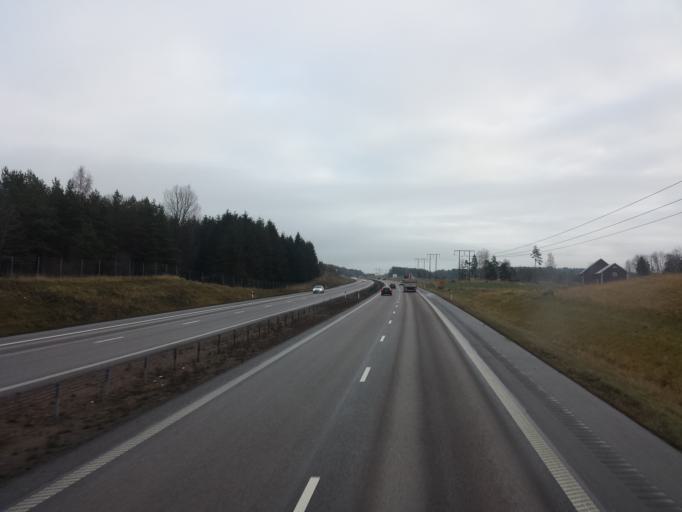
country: SE
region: OEstergoetland
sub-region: Norrkopings Kommun
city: Skarblacka
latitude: 58.4820
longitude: 15.8883
